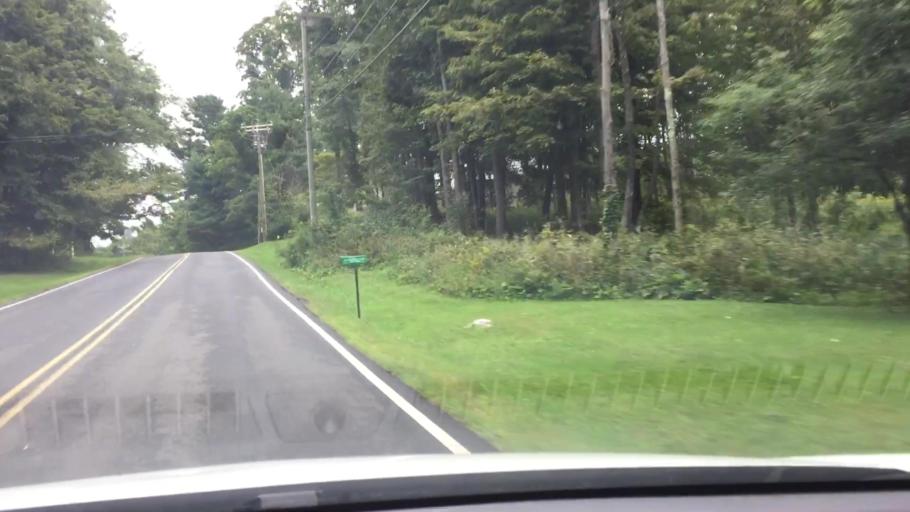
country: US
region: Massachusetts
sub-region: Berkshire County
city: Richmond
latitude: 42.3995
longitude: -73.3334
